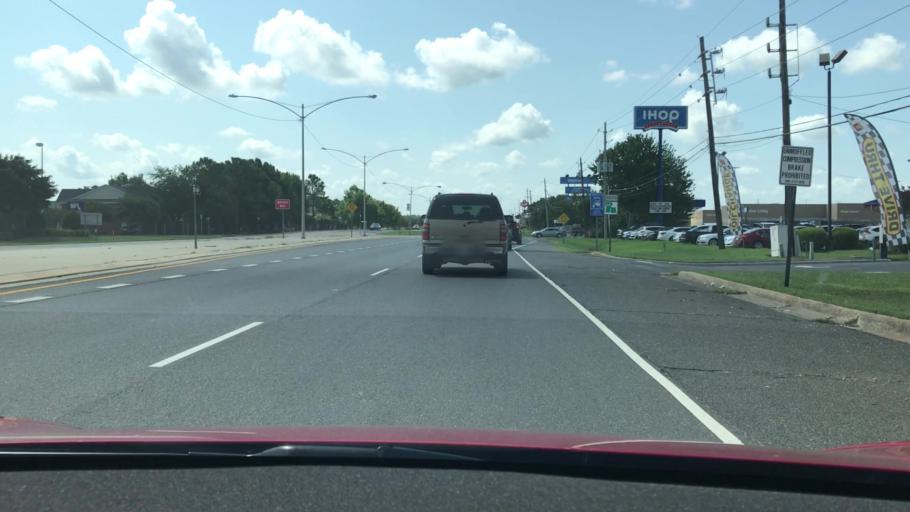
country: US
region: Louisiana
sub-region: Bossier Parish
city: Bossier City
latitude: 32.4314
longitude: -93.7118
